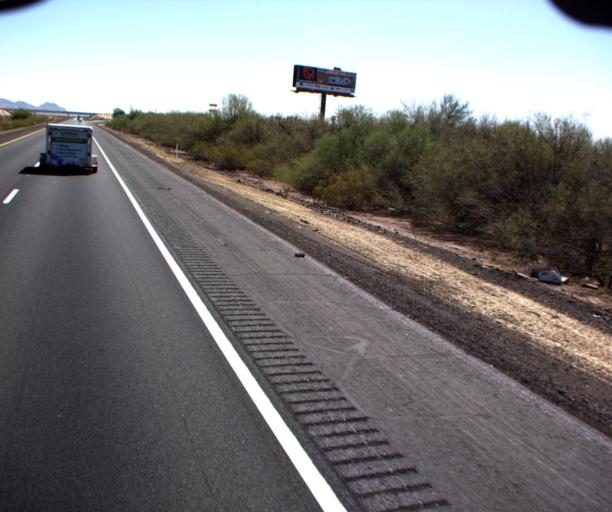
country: US
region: Arizona
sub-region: La Paz County
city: Salome
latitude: 33.6319
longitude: -113.7757
